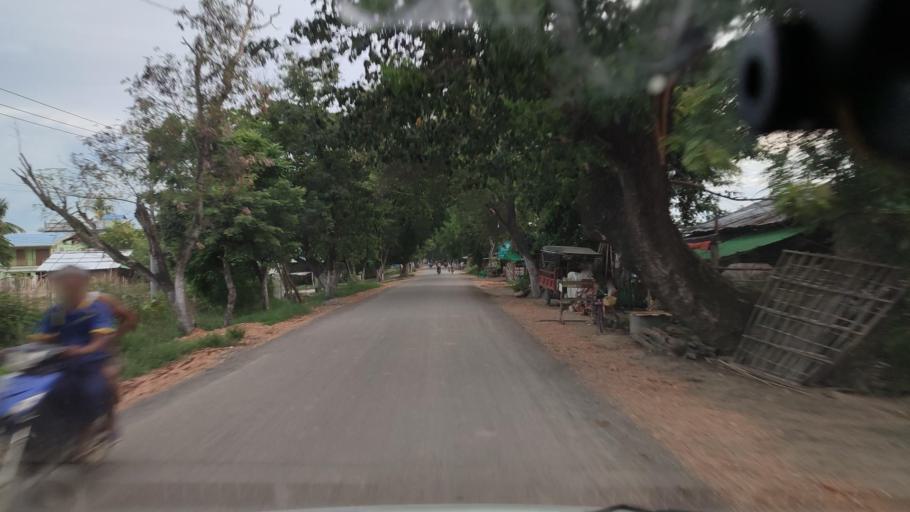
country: MM
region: Magway
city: Yenangyaung
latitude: 20.3625
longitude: 94.7664
